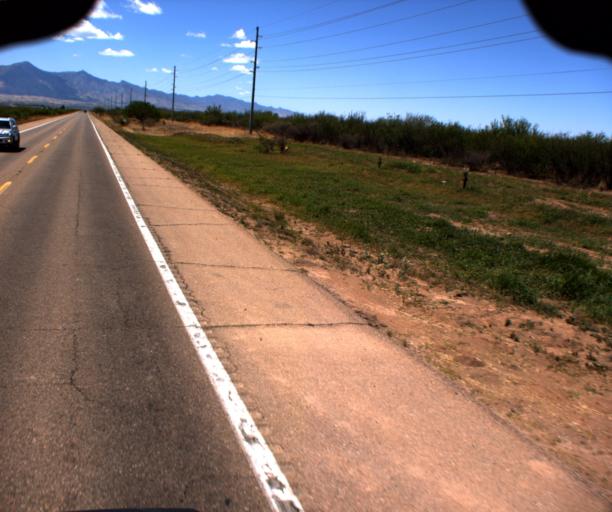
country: US
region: Arizona
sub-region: Cochise County
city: Naco
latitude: 31.3777
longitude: -110.0207
